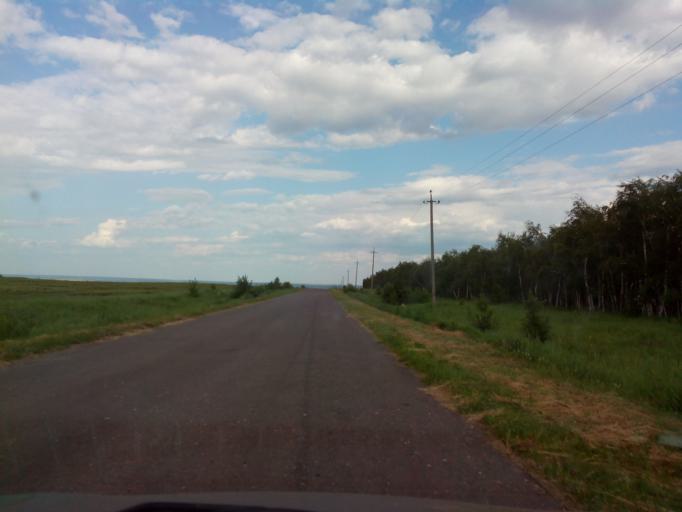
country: RU
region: Volgograd
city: Slashchevskaya
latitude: 49.7959
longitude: 42.4108
